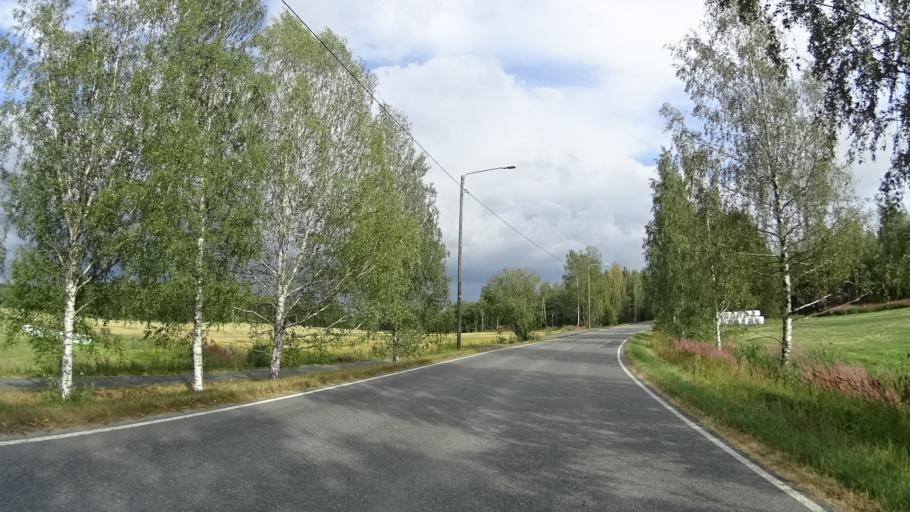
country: FI
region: Pirkanmaa
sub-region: Etelae-Pirkanmaa
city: Valkeakoski
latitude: 61.2113
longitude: 24.0560
